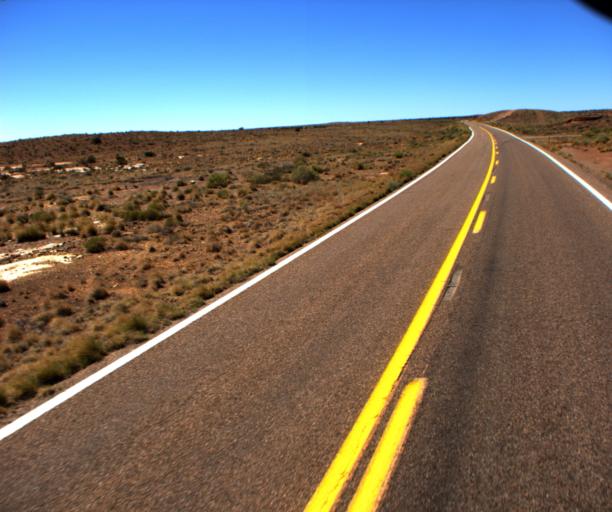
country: US
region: Arizona
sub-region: Navajo County
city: Winslow
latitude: 34.9598
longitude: -110.6474
